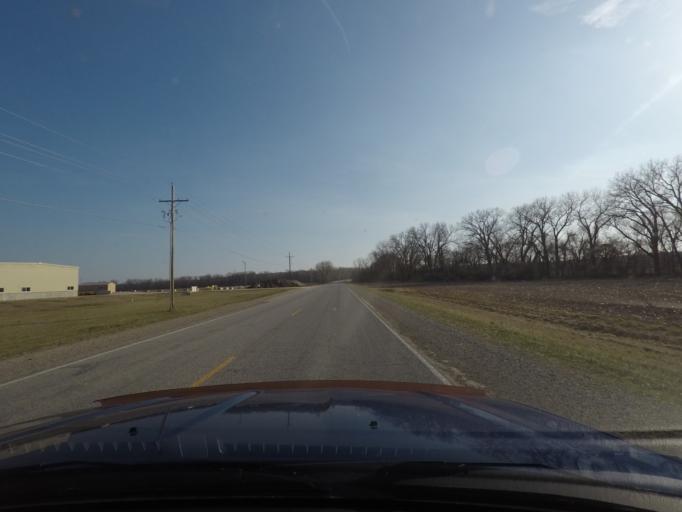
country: US
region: Kansas
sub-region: Douglas County
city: Lawrence
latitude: 39.0569
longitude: -95.3836
